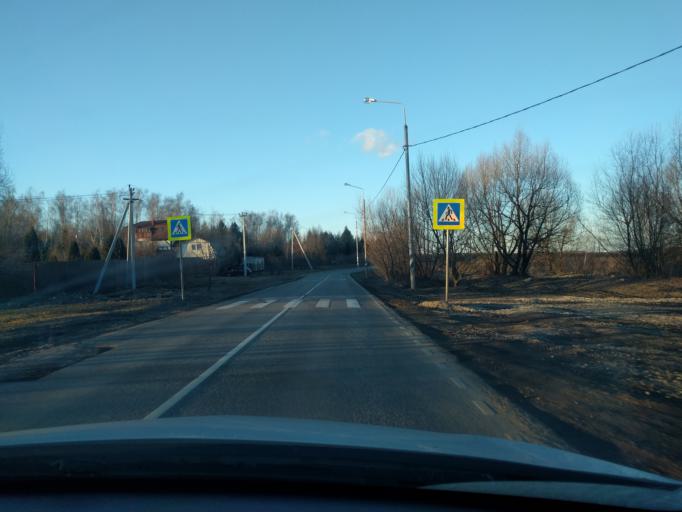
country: RU
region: Moskovskaya
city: Vatutinki
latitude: 55.4899
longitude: 37.4158
